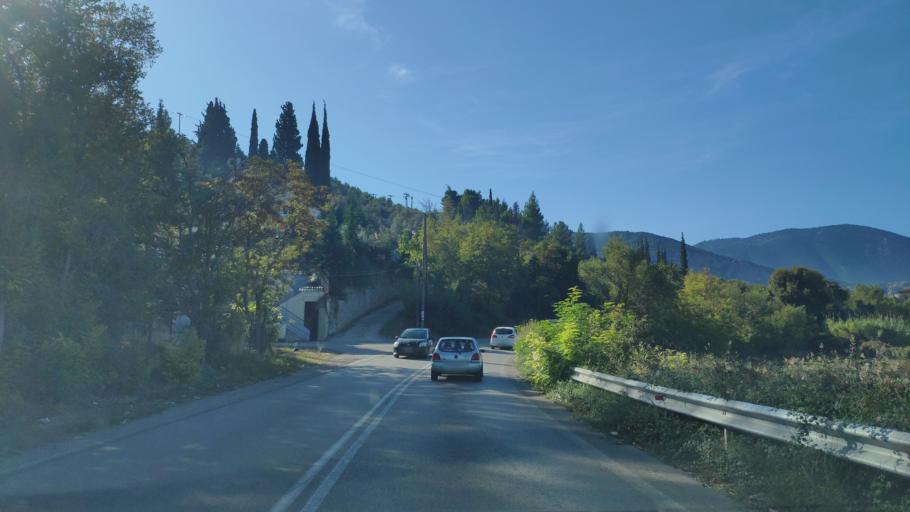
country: GR
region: Central Greece
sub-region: Nomos Voiotias
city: Livadeia
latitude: 38.4496
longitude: 22.8821
